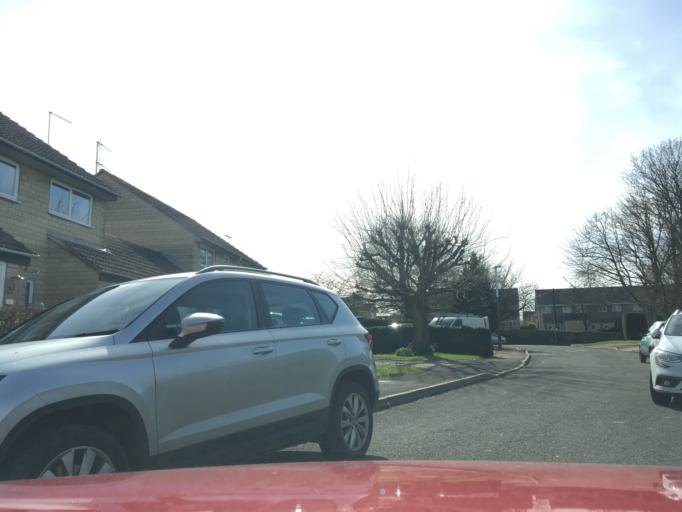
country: GB
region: England
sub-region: Wiltshire
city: Chippenham
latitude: 51.4976
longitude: -2.1422
